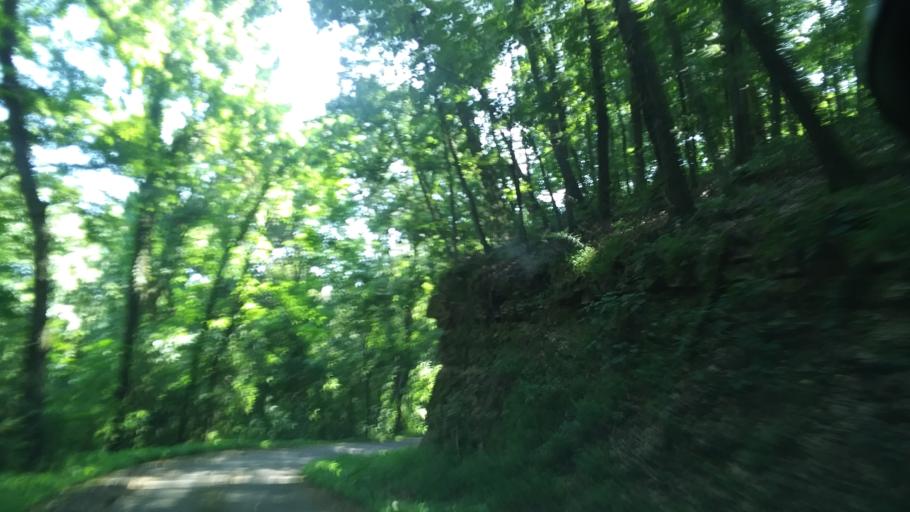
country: US
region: Tennessee
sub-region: Davidson County
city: Belle Meade
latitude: 36.0663
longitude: -86.8924
